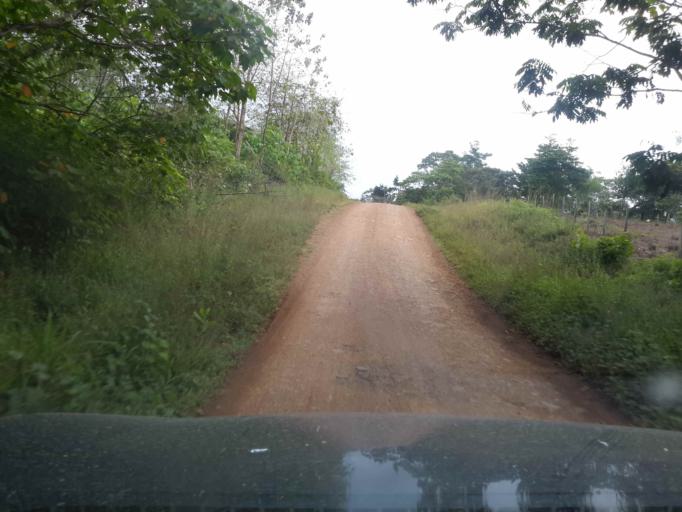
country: CR
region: Alajuela
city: Los Chiles
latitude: 11.0583
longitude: -84.4855
